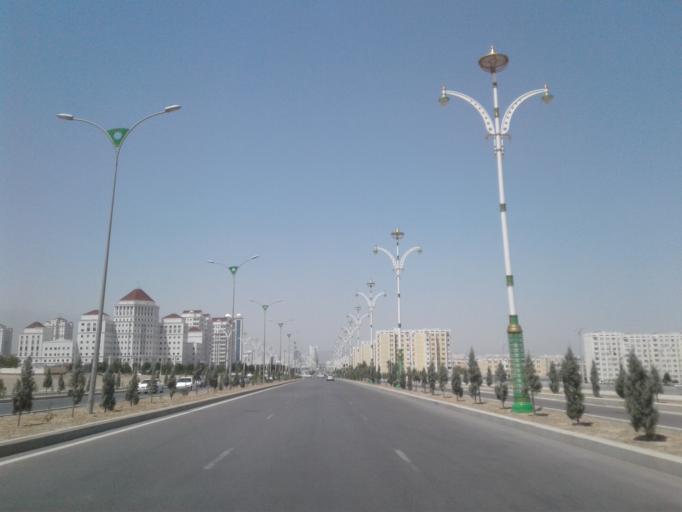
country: TM
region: Ahal
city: Ashgabat
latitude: 37.8954
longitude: 58.4012
